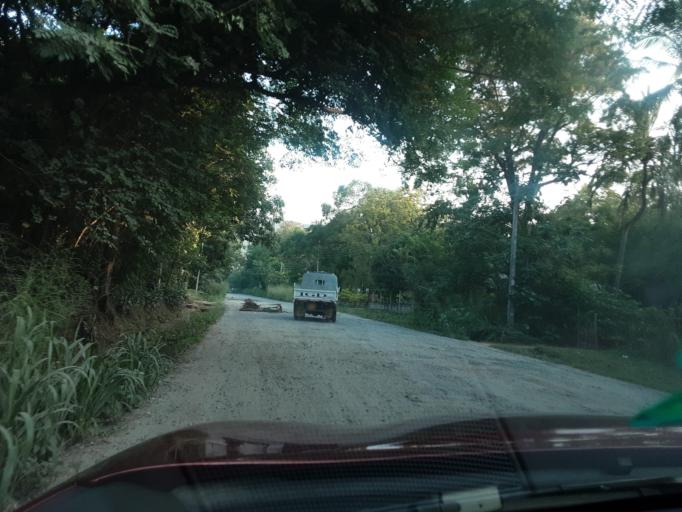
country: LK
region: Central
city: Dambulla
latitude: 7.8571
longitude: 80.6817
